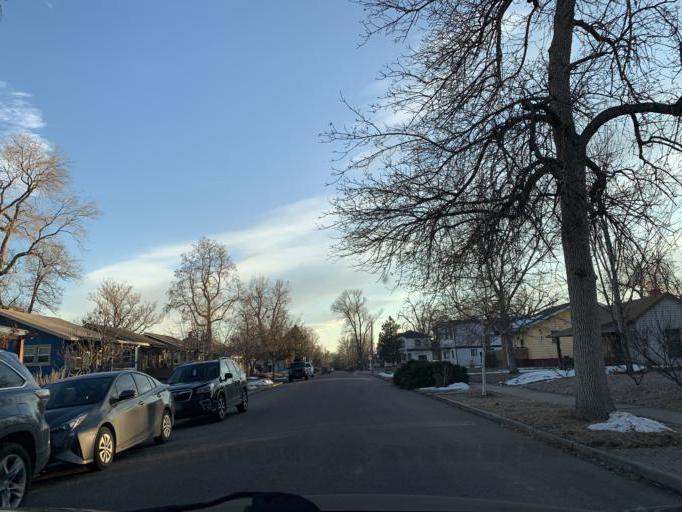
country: US
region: Colorado
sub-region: Adams County
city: Berkley
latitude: 39.7865
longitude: -105.0358
